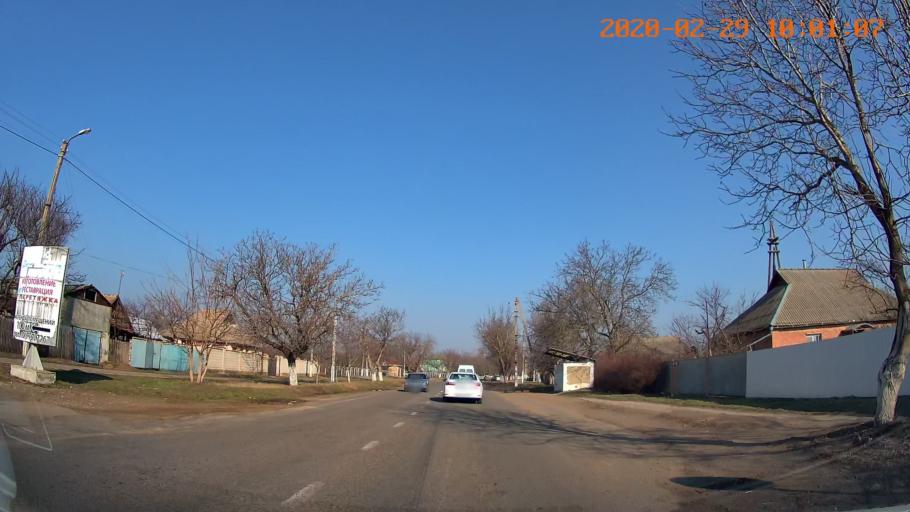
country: MD
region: Telenesti
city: Slobozia
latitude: 46.7731
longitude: 29.6852
